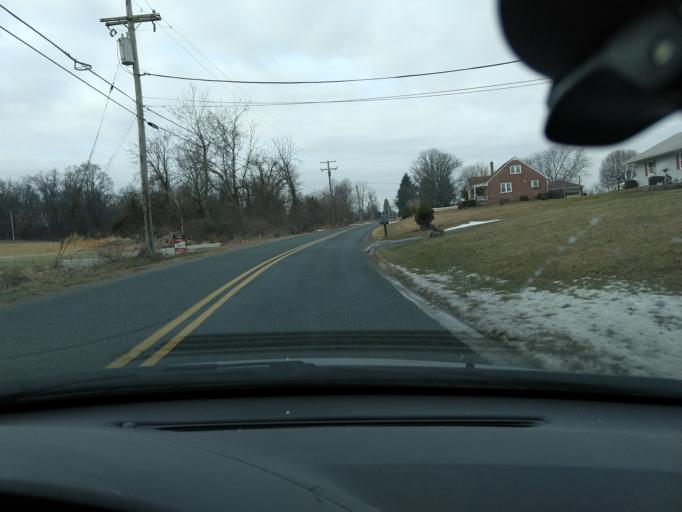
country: US
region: Pennsylvania
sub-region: Berks County
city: Amity Gardens
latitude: 40.2414
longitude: -75.7624
